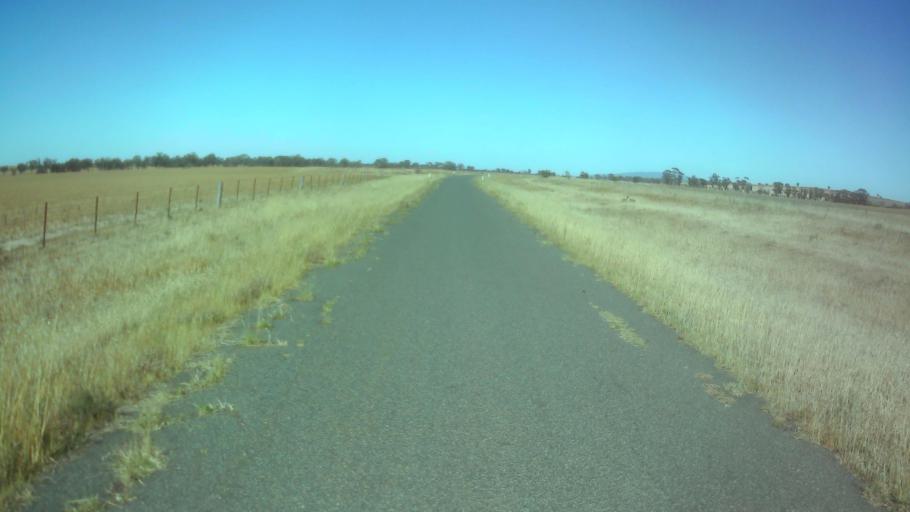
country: AU
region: New South Wales
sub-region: Weddin
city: Grenfell
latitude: -33.9960
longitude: 148.3859
